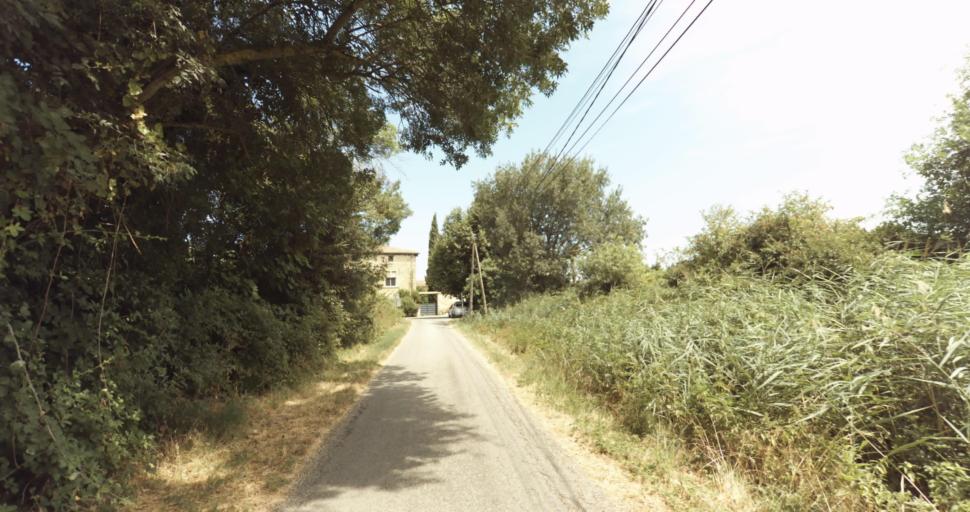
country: FR
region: Provence-Alpes-Cote d'Azur
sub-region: Departement du Vaucluse
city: Althen-des-Paluds
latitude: 44.0298
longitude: 4.9398
